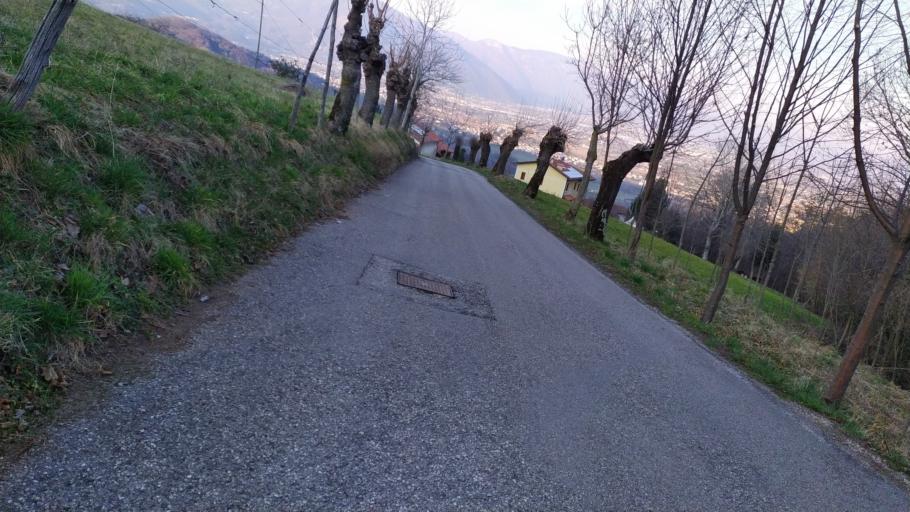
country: IT
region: Veneto
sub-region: Provincia di Vicenza
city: Monte di Malo
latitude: 45.6720
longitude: 11.3503
